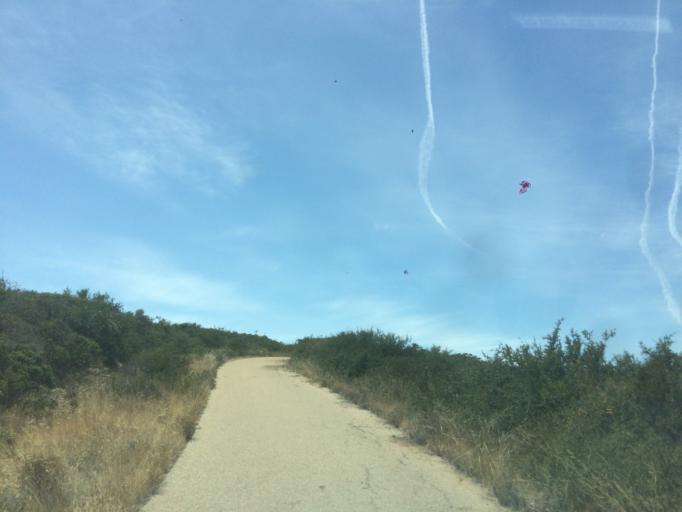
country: US
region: California
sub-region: San Luis Obispo County
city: San Luis Obispo
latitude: 35.2536
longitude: -120.7076
